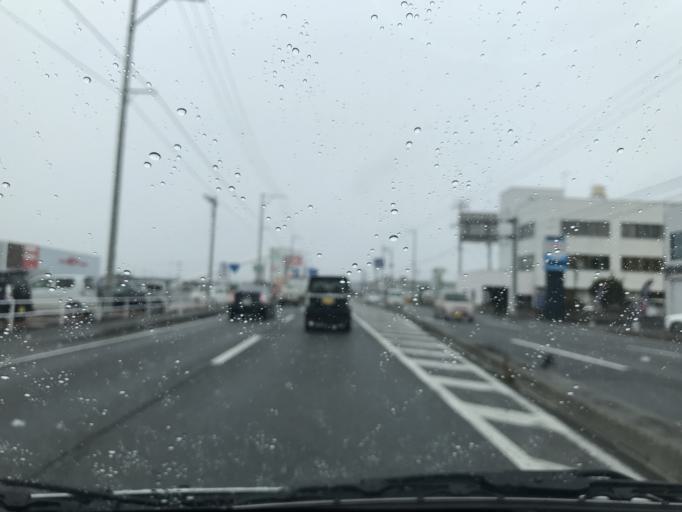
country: JP
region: Iwate
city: Kitakami
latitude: 39.2737
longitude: 141.1010
